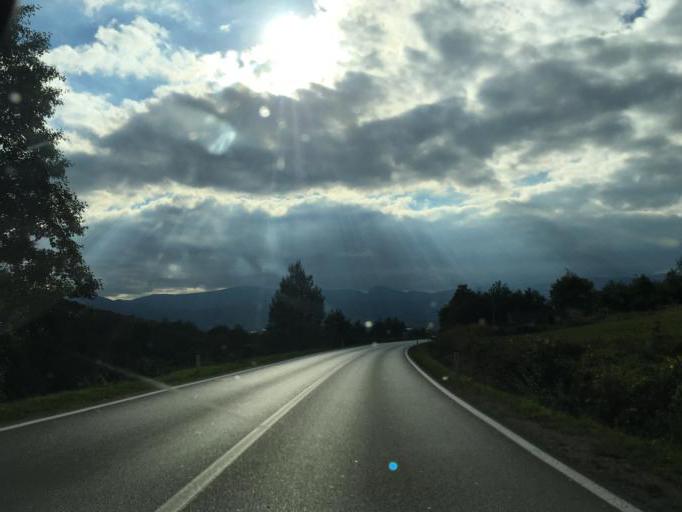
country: BA
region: Federation of Bosnia and Herzegovina
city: Bugojno
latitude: 44.0704
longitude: 17.4931
